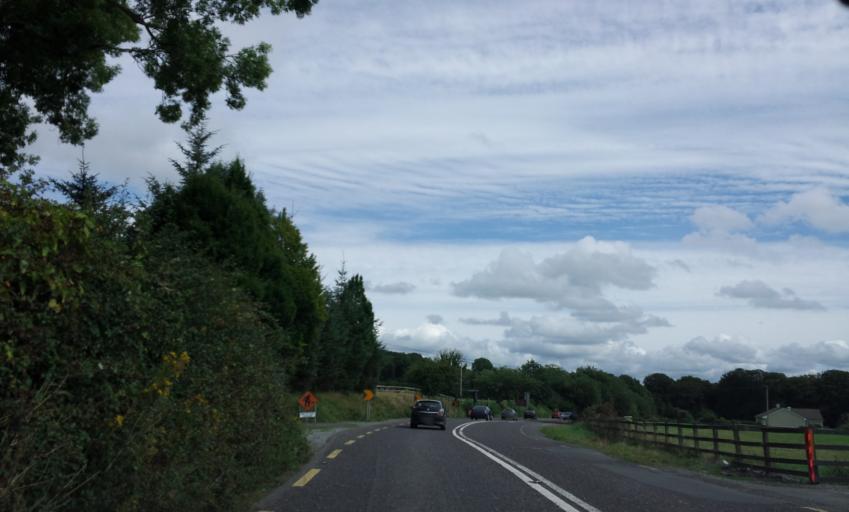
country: IE
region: Munster
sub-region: Ciarrai
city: Cill Airne
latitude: 52.0720
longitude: -9.5988
